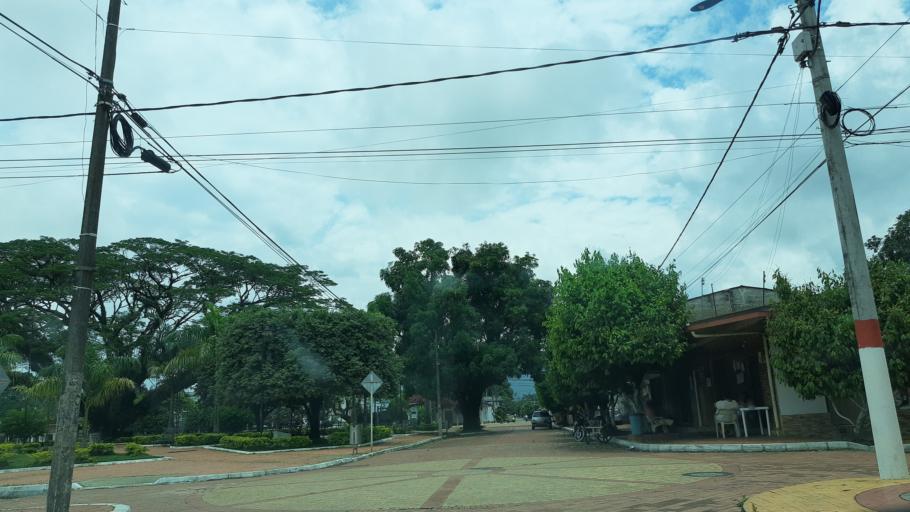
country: CO
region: Casanare
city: Sabanalarga
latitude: 4.8539
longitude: -73.0407
